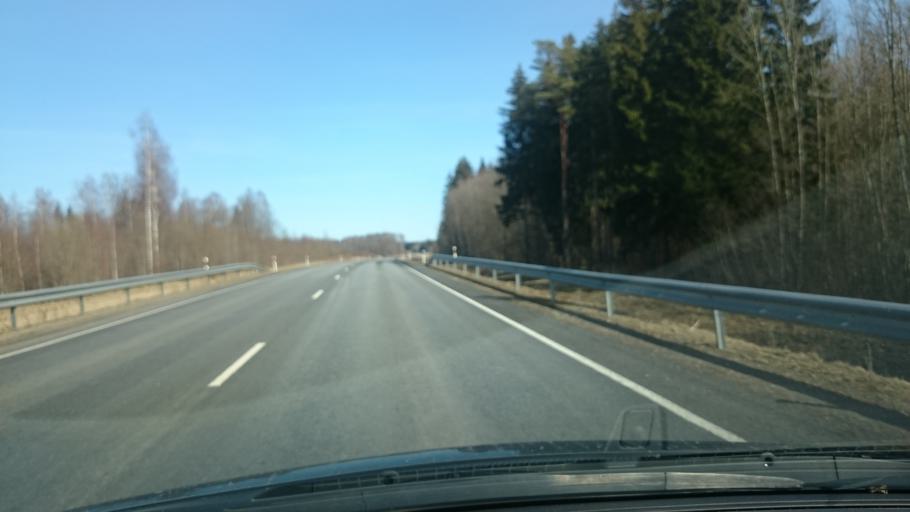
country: EE
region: Paernumaa
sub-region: Vaendra vald (alev)
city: Vandra
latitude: 58.6428
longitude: 24.9721
